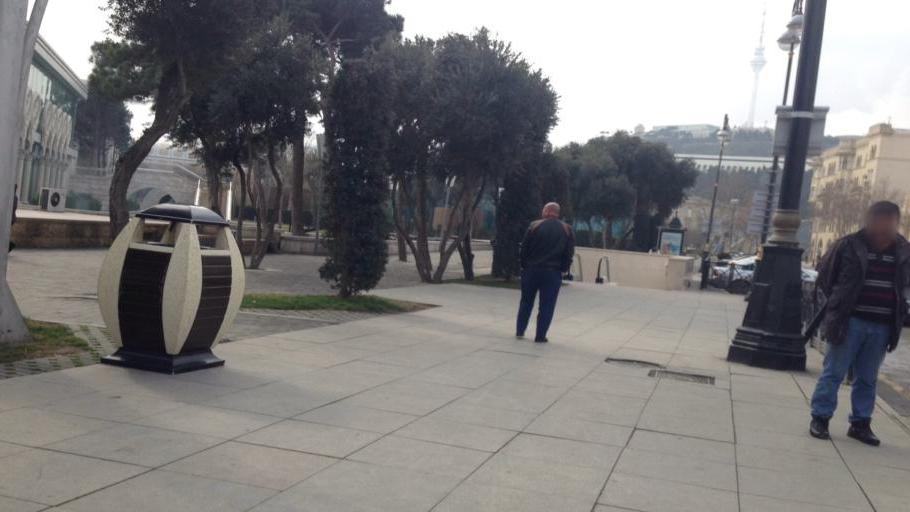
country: AZ
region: Baki
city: Badamdar
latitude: 40.3622
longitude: 49.8358
